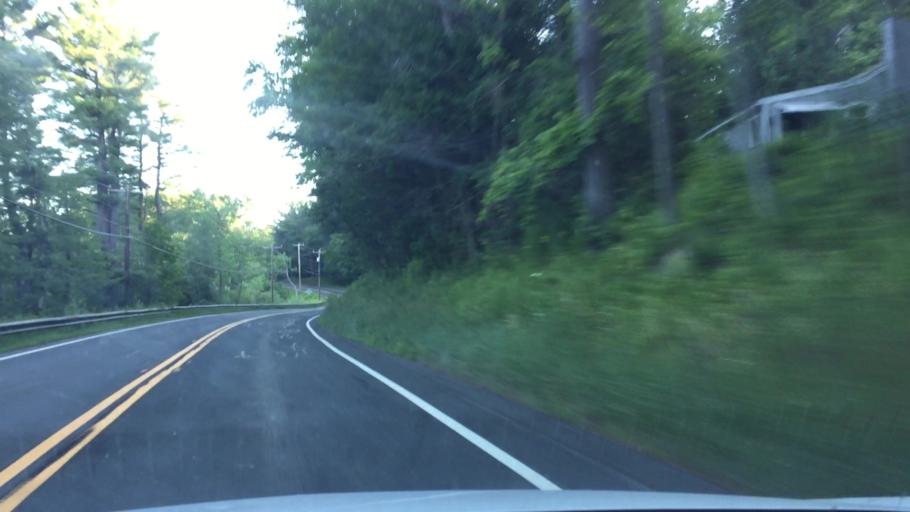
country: US
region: Massachusetts
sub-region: Berkshire County
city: Otis
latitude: 42.2198
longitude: -73.1026
